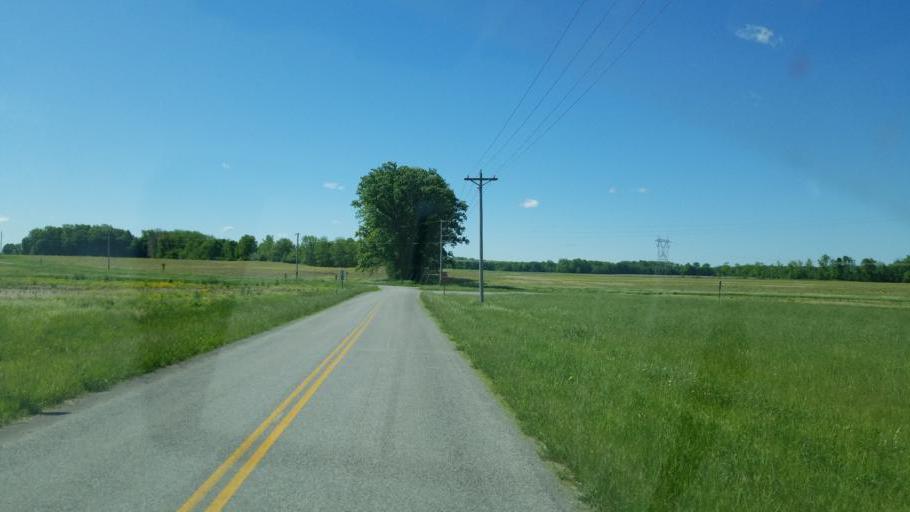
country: US
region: Ohio
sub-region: Logan County
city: Northwood
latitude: 40.4402
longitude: -83.6761
